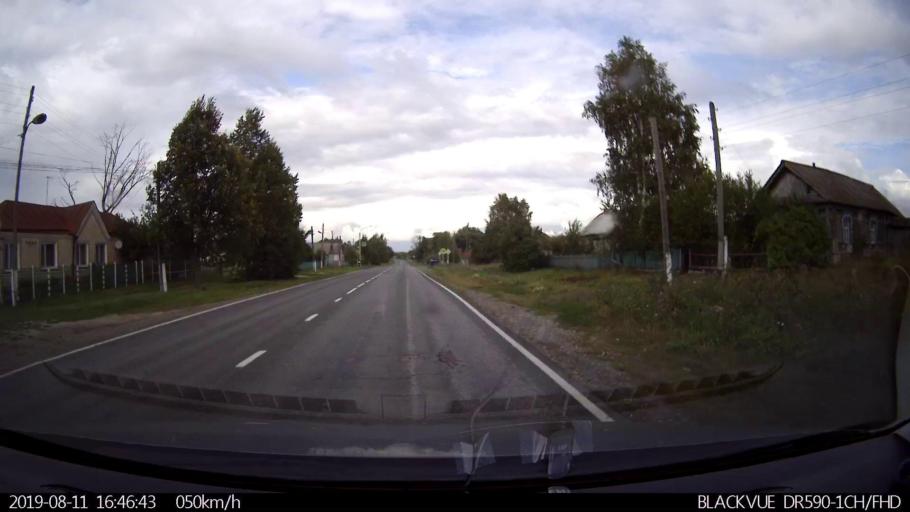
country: RU
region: Ulyanovsk
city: Mayna
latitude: 54.1993
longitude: 47.6909
